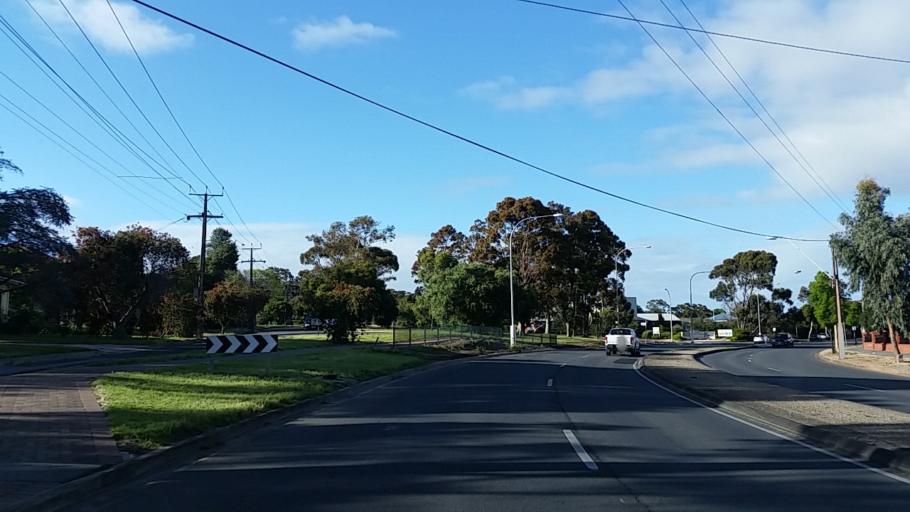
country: AU
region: South Australia
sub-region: Mitcham
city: Clapham
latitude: -34.9990
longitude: 138.5933
